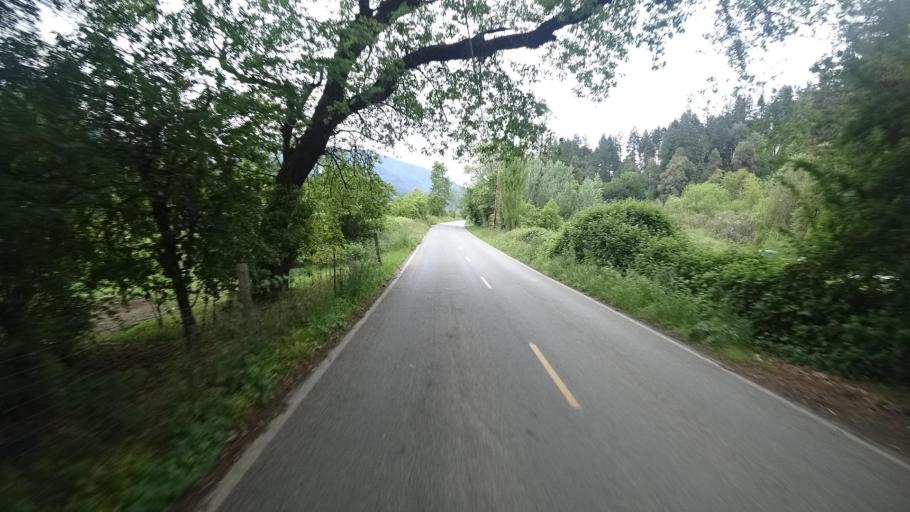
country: US
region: California
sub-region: Humboldt County
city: Willow Creek
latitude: 41.0780
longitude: -123.6978
